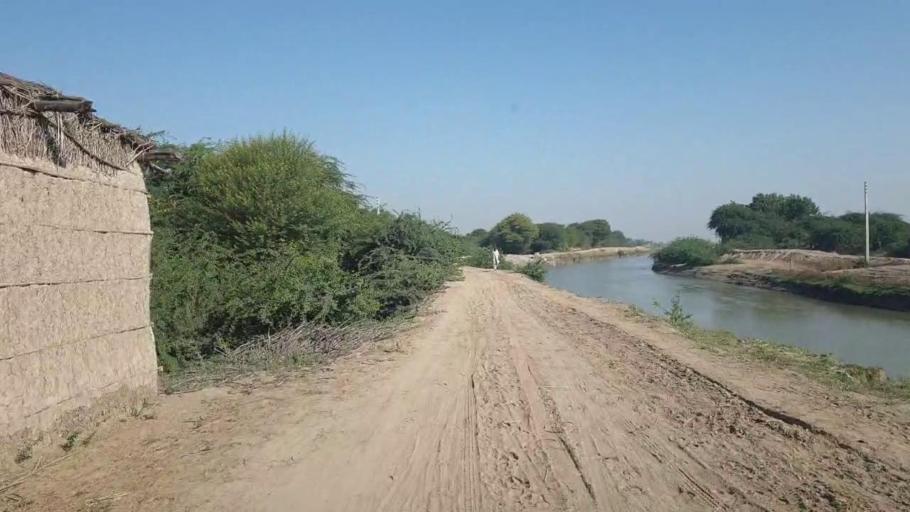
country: PK
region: Sindh
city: Badin
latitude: 24.7229
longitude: 68.8030
